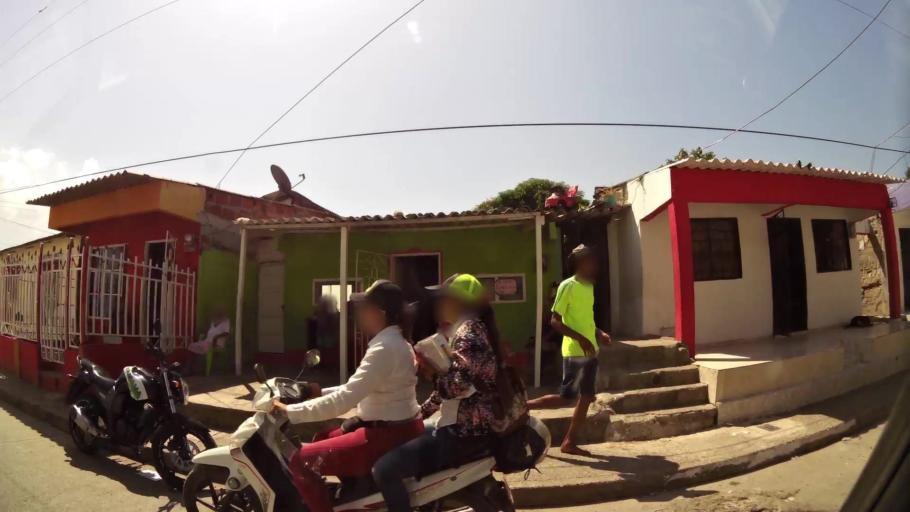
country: CO
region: Bolivar
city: Cartagena
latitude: 10.3842
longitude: -75.5013
